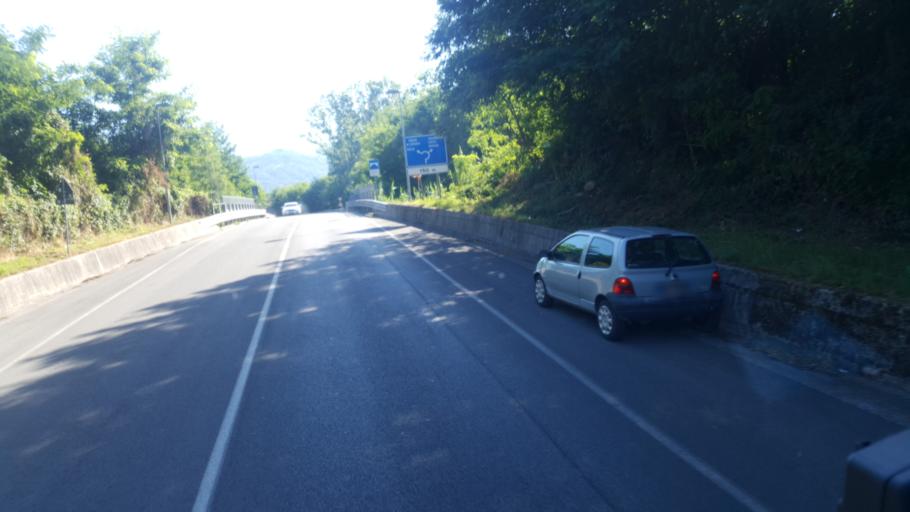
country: IT
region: Tuscany
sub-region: Provincia di Lucca
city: Castelnuovo di Garfagnana
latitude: 44.1238
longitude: 10.3964
